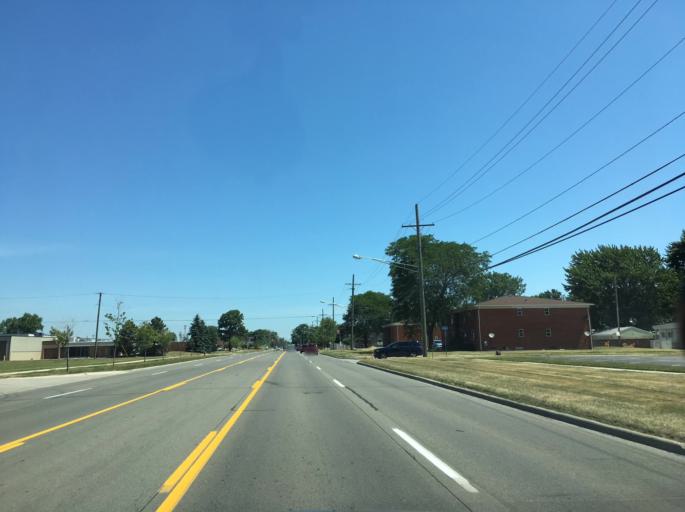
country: US
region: Michigan
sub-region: Macomb County
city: Saint Clair Shores
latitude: 42.5373
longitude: -82.8843
